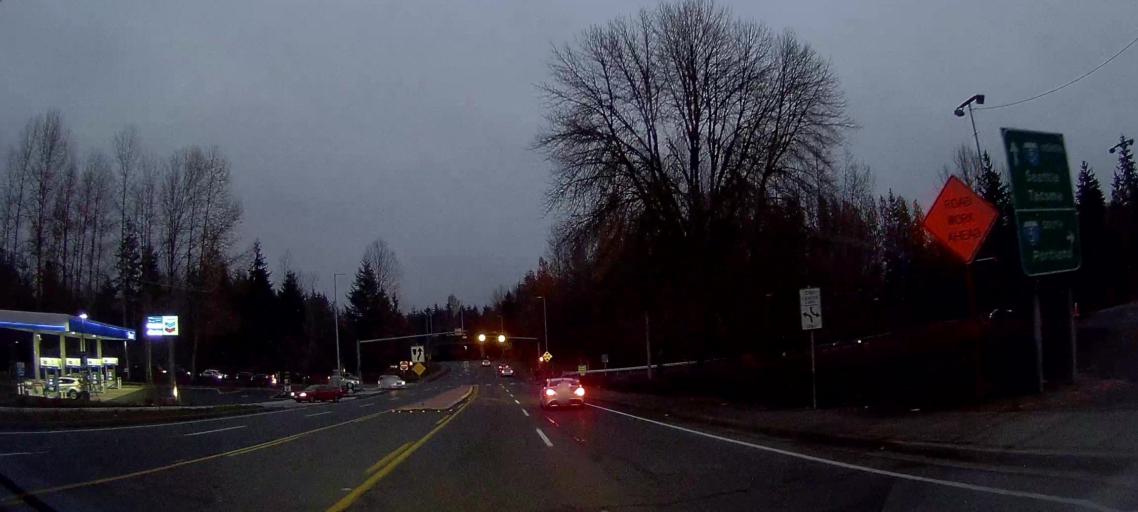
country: US
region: Washington
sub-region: Thurston County
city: Lacey
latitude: 47.0421
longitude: -122.8547
